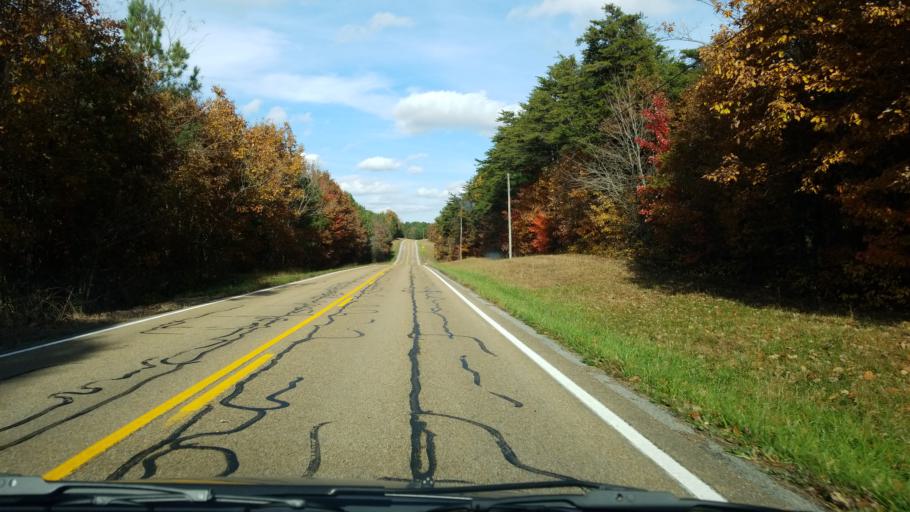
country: US
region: Tennessee
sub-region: Sequatchie County
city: Dunlap
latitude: 35.4530
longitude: -85.5004
